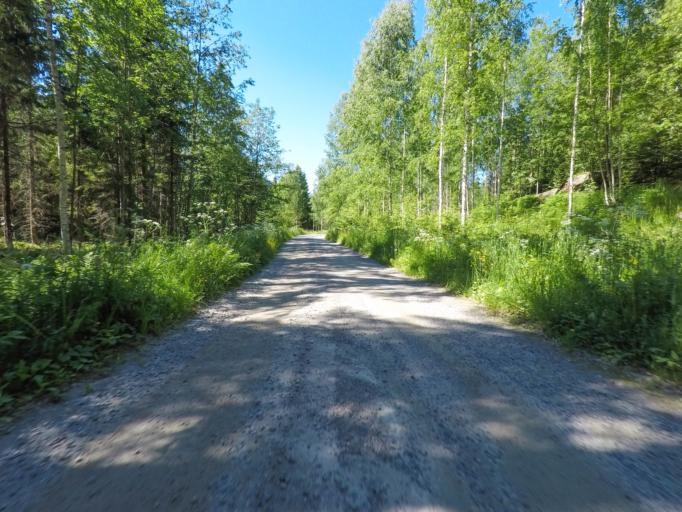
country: FI
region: Northern Savo
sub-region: Varkaus
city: Kangaslampi
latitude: 62.1740
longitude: 28.2407
